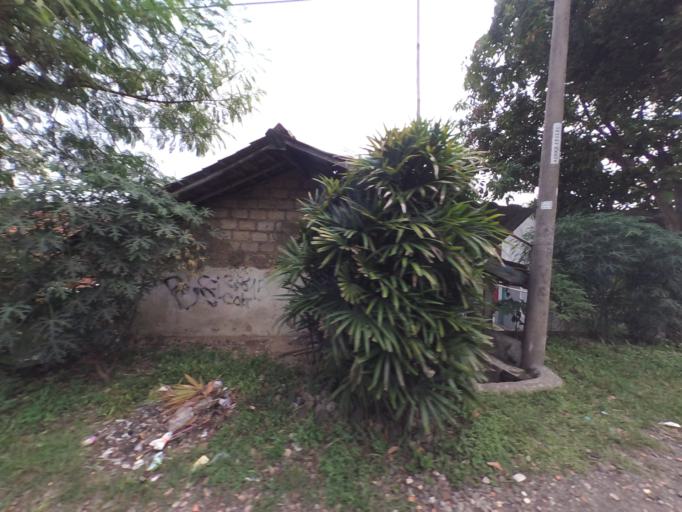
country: ID
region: West Java
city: Ciampea
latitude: -6.5593
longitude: 106.6867
